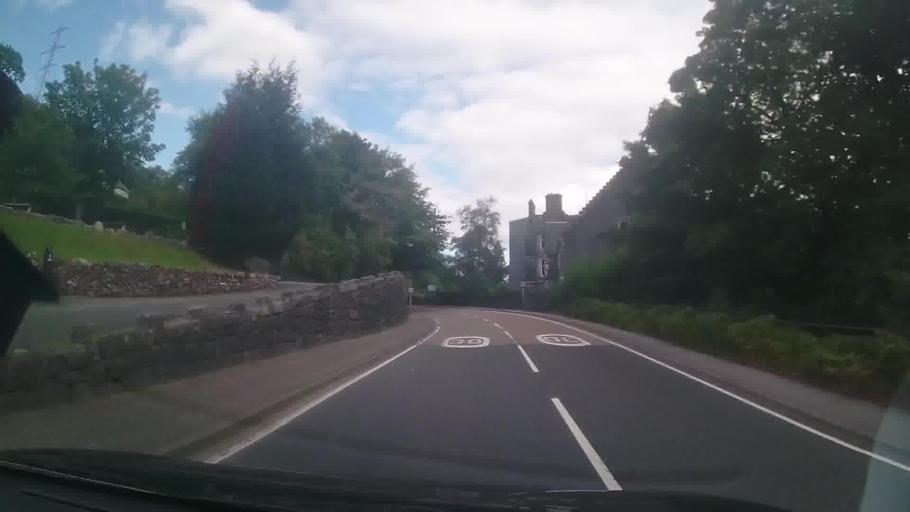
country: GB
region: Scotland
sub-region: Argyll and Bute
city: Garelochhead
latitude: 56.4020
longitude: -5.0448
